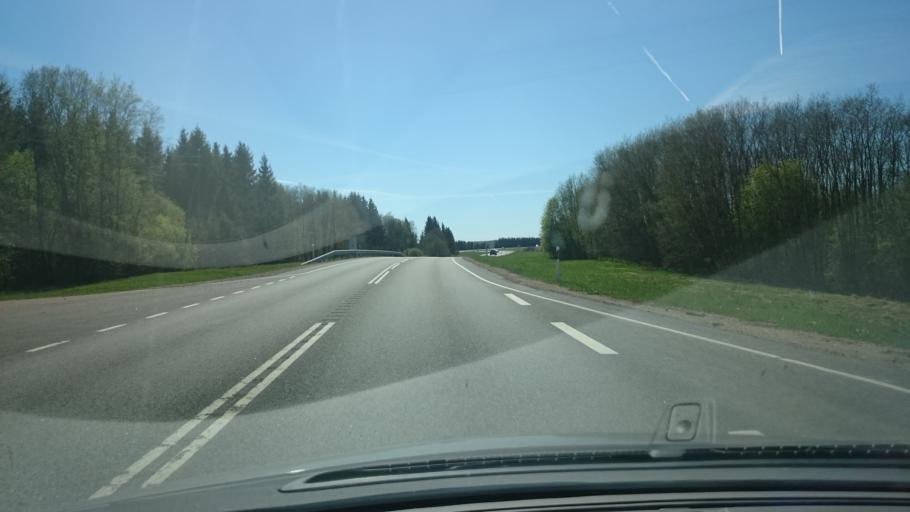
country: EE
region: Ida-Virumaa
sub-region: Narva-Joesuu linn
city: Narva-Joesuu
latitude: 59.3788
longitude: 27.9576
